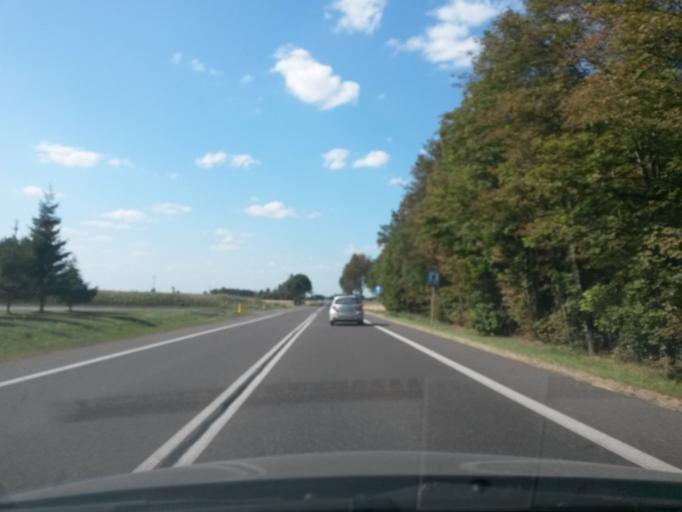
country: PL
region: Masovian Voivodeship
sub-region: Powiat plocki
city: Starozreby
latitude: 52.6651
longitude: 20.0745
